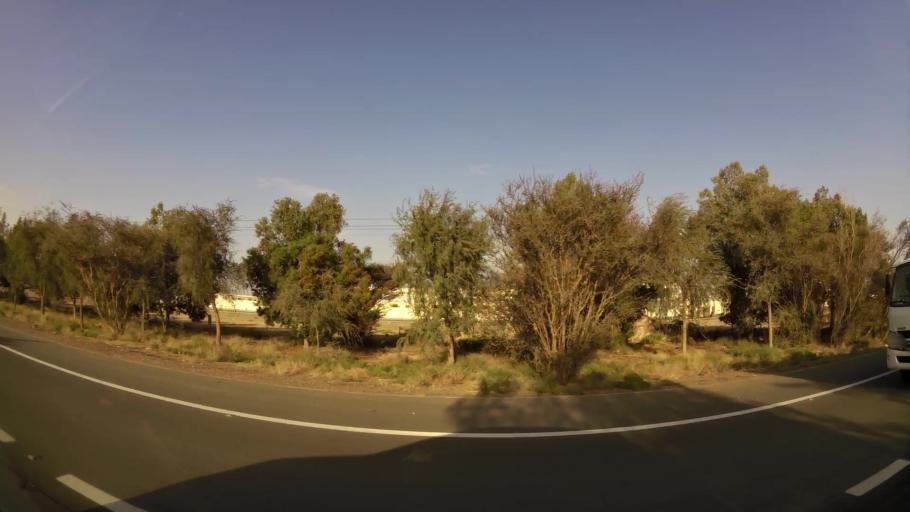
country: AE
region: Abu Dhabi
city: Al Ain
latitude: 24.1335
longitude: 55.8184
